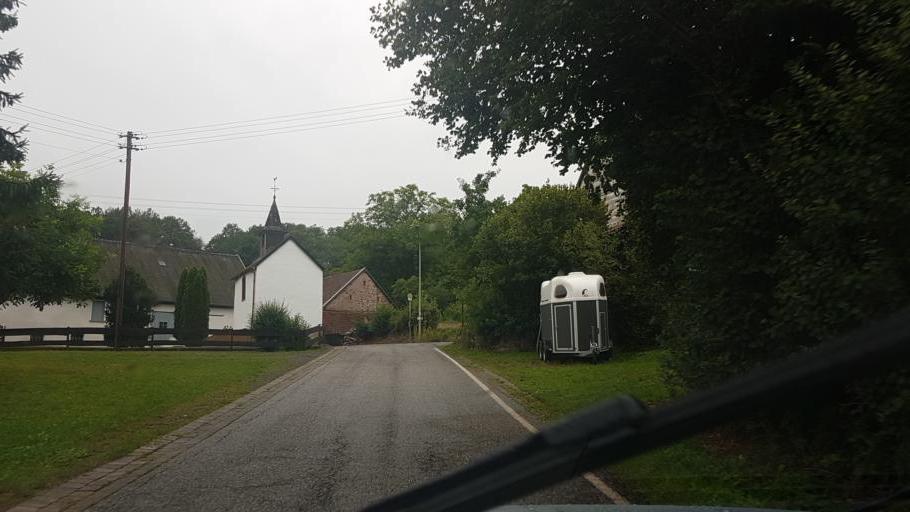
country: DE
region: Saarland
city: Wadern
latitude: 49.5461
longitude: 6.9113
